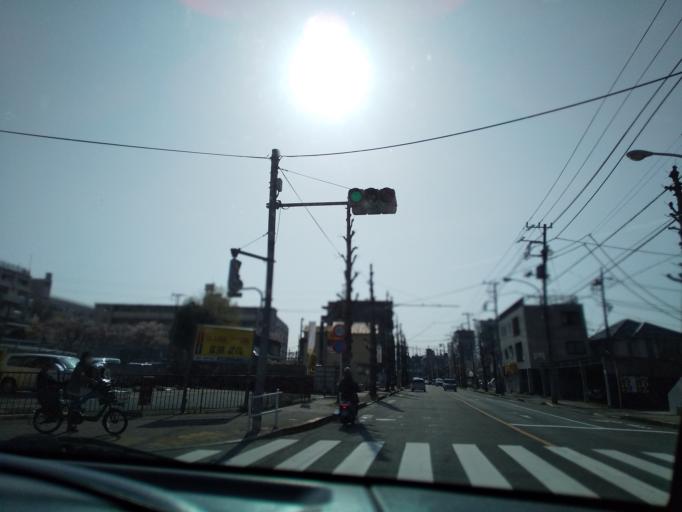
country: JP
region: Tokyo
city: Hino
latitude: 35.7054
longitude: 139.3819
